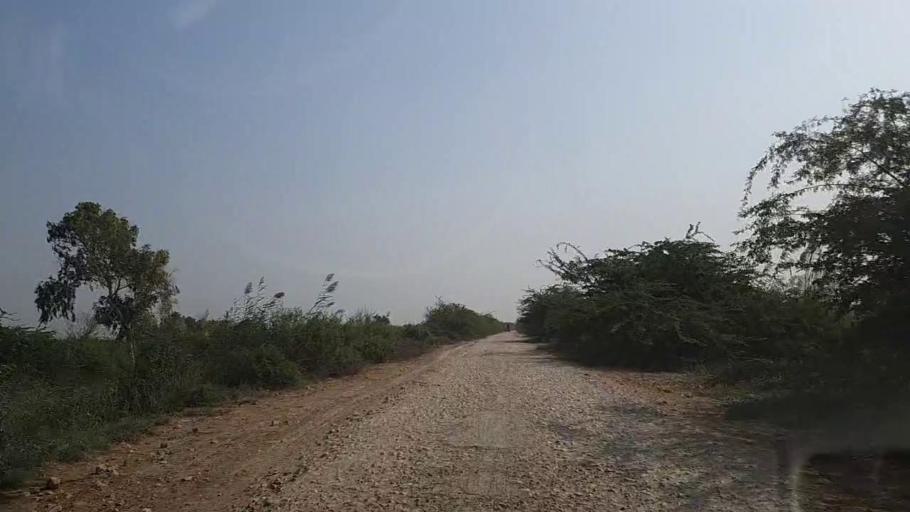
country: PK
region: Sindh
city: Keti Bandar
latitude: 24.2494
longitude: 67.6311
